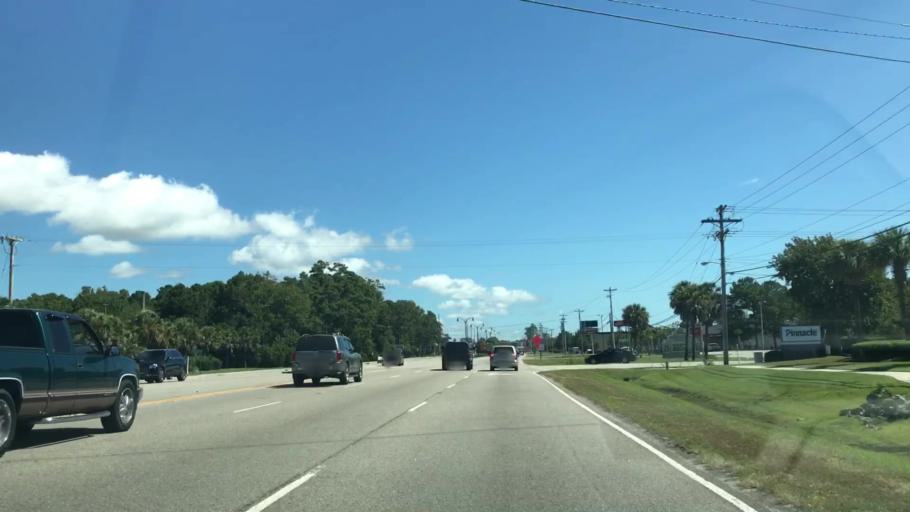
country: US
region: South Carolina
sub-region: Horry County
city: North Myrtle Beach
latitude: 33.8342
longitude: -78.6723
